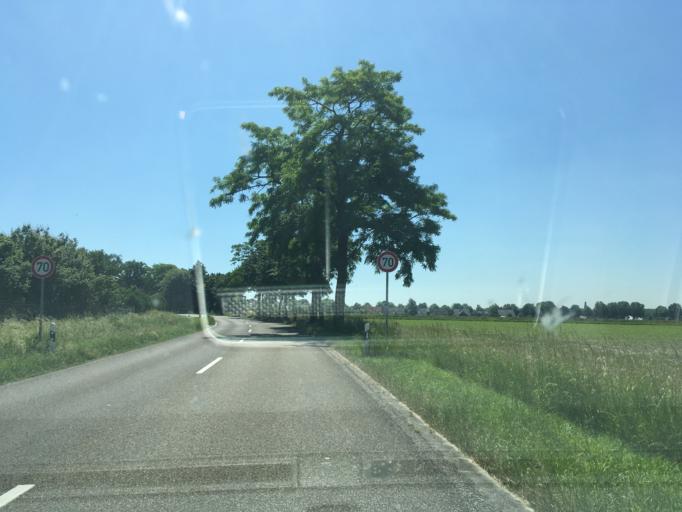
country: DE
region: North Rhine-Westphalia
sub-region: Regierungsbezirk Munster
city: Raesfeld
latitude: 51.7763
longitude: 6.8286
